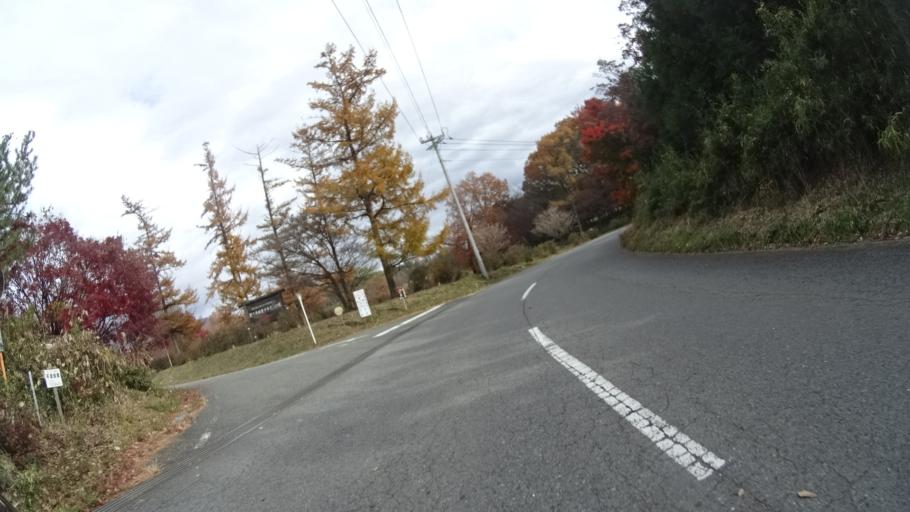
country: JP
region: Gunma
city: Maebashi-shi
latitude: 36.4774
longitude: 139.1243
